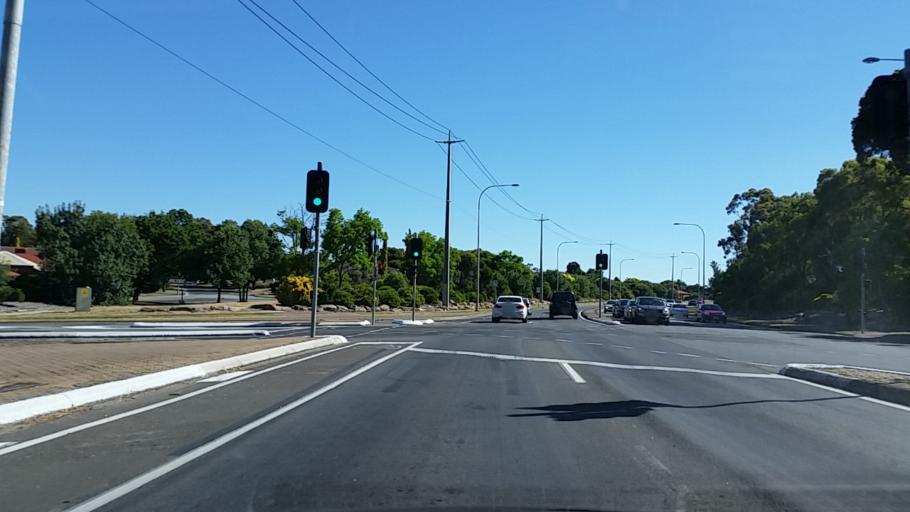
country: AU
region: South Australia
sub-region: Tea Tree Gully
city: Modbury
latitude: -34.8036
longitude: 138.6848
